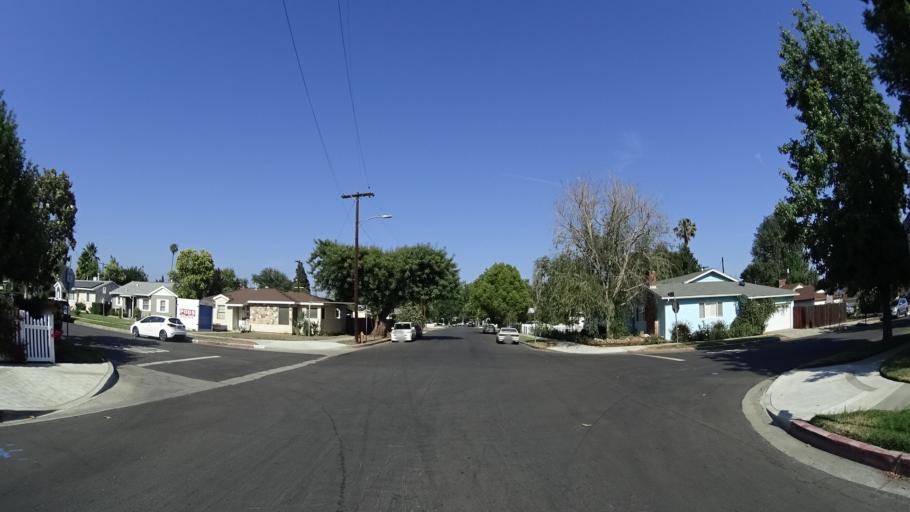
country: US
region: California
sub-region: Los Angeles County
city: Sherman Oaks
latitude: 34.1685
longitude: -118.4566
